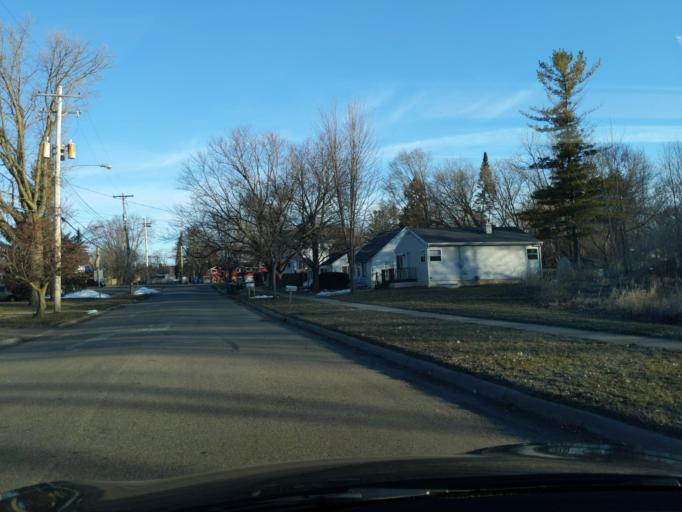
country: US
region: Michigan
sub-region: Ingham County
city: Lansing
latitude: 42.6964
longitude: -84.5631
